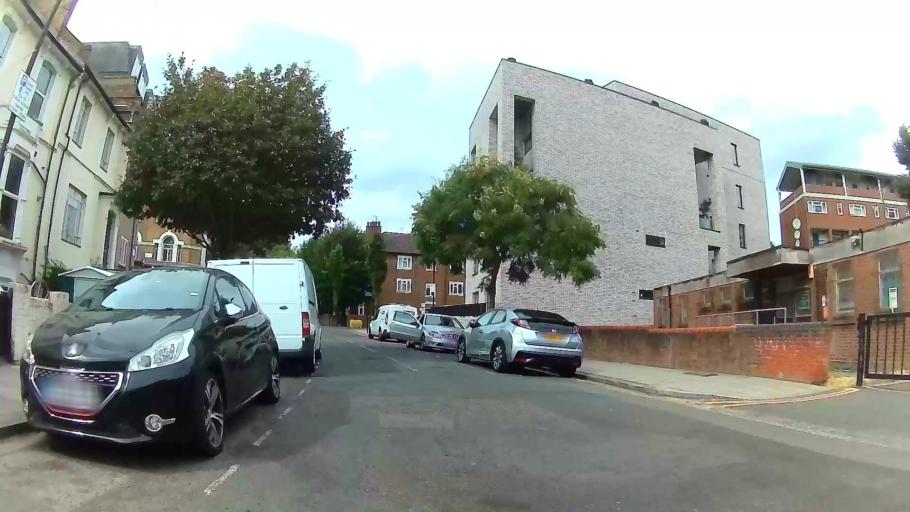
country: GB
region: England
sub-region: Greater London
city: Hackney
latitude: 51.5555
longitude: -0.0679
